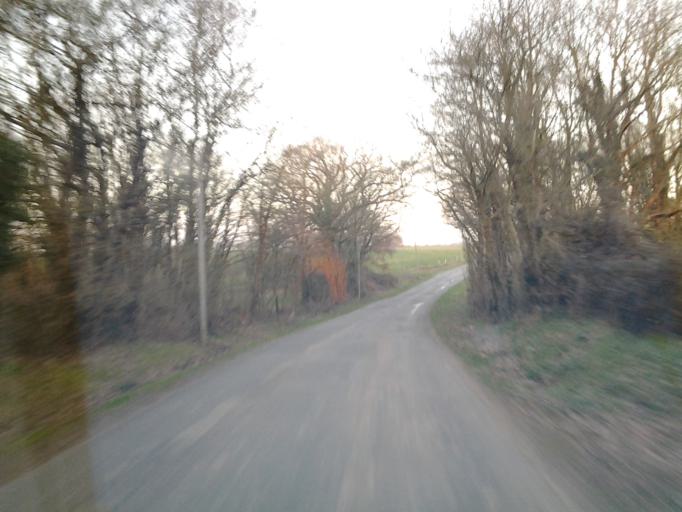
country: FR
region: Pays de la Loire
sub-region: Departement de la Vendee
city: La Chaize-le-Vicomte
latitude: 46.6605
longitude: -1.2390
